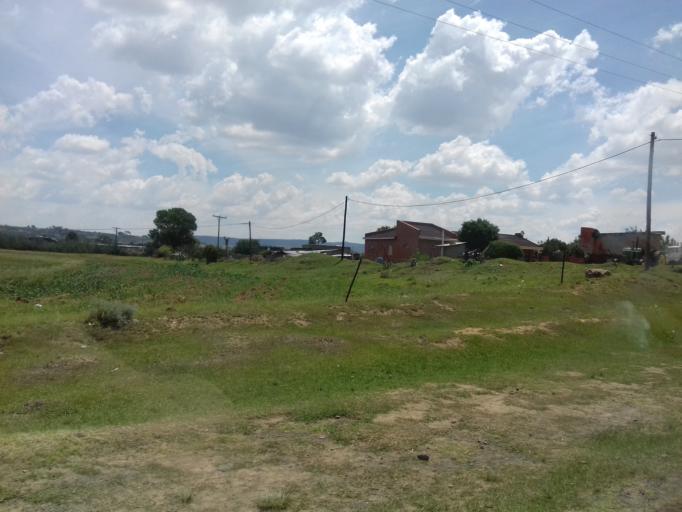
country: LS
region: Maseru
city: Nako
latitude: -29.5975
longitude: 27.5622
